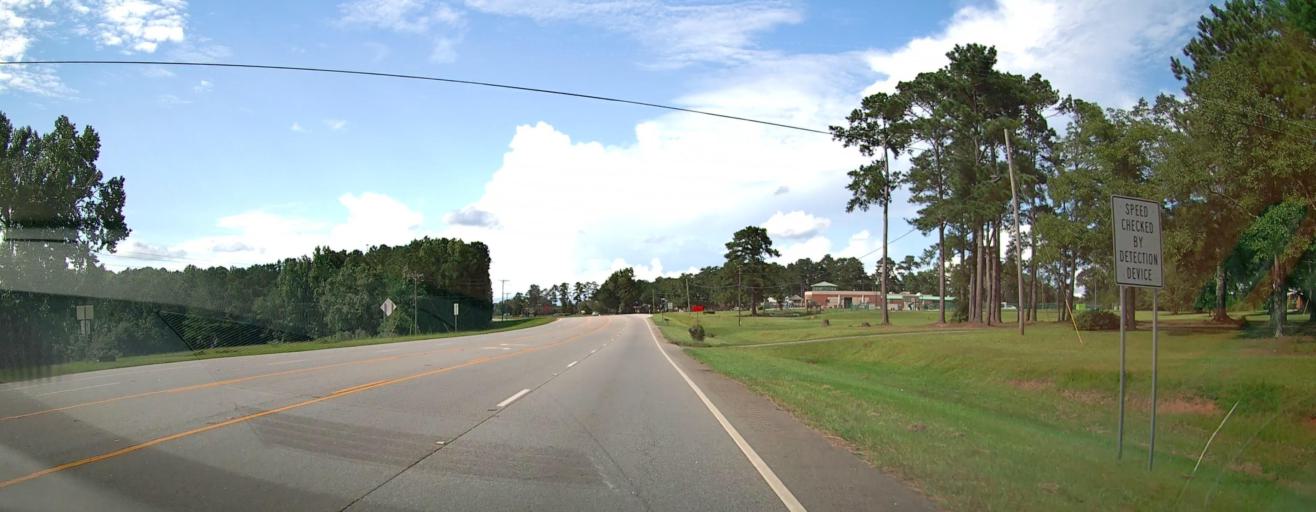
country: US
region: Georgia
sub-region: Upson County
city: Thomaston
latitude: 32.8595
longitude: -84.3178
